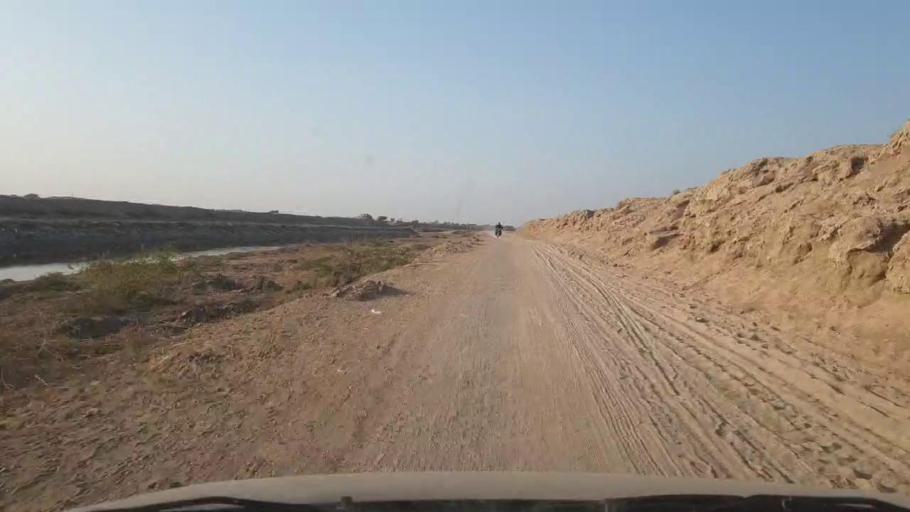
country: PK
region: Sindh
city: Samaro
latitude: 25.2914
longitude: 69.3327
